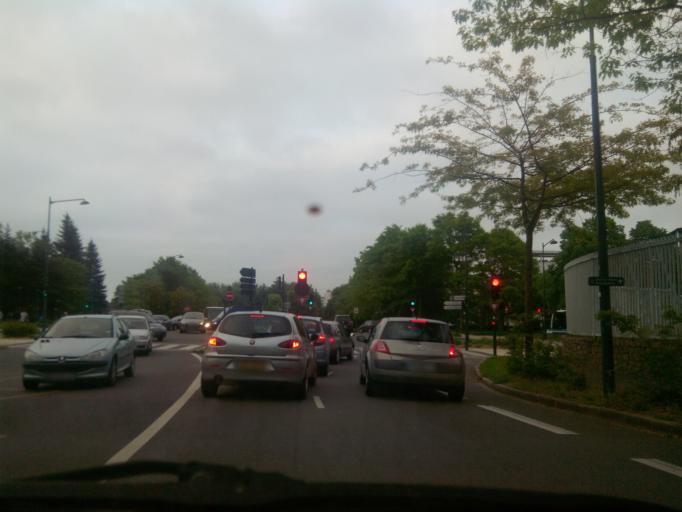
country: FR
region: Brittany
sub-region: Departement d'Ille-et-Vilaine
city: Rennes
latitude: 48.1267
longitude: -1.6931
